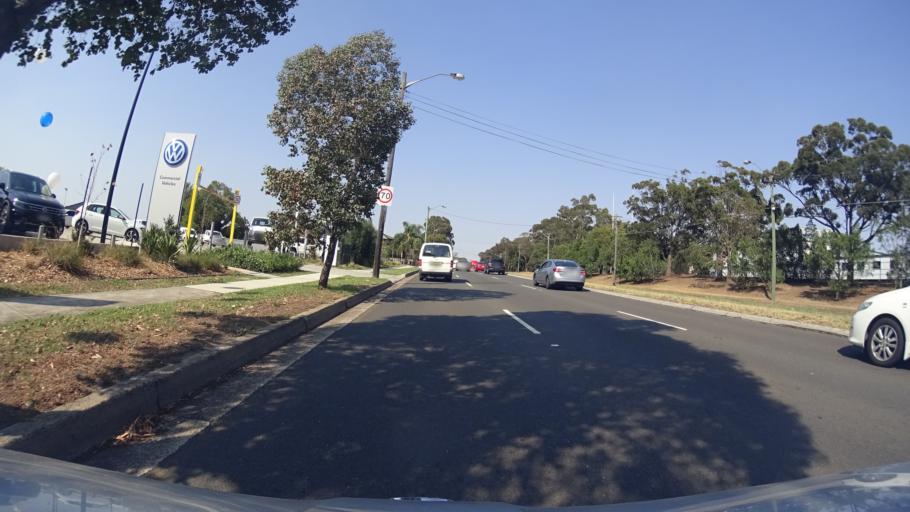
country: AU
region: New South Wales
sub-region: Bankstown
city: Bankstown
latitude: -33.8950
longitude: 151.0531
